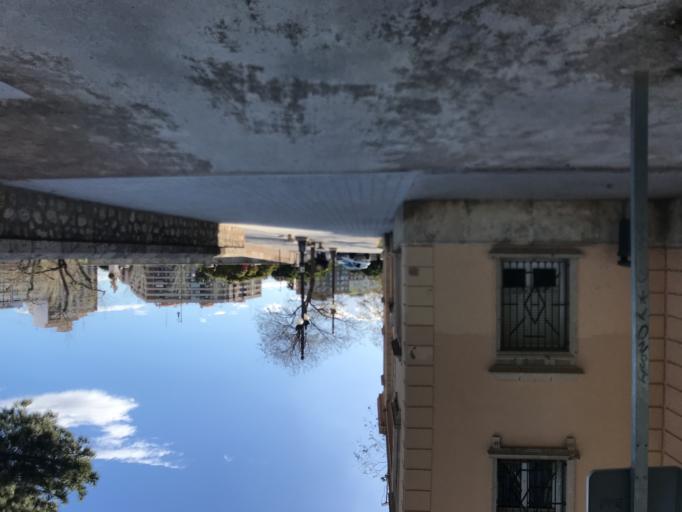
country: ES
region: Valencia
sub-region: Provincia de Valencia
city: Valencia
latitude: 39.4813
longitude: -0.3795
